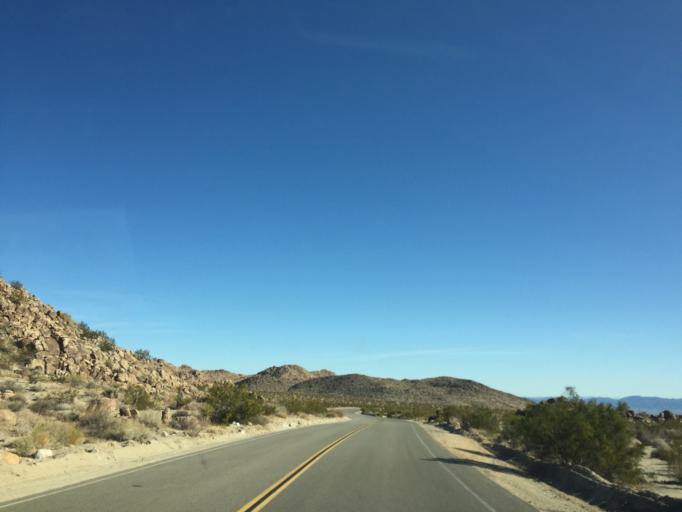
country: US
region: California
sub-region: Riverside County
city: Mecca
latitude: 33.8121
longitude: -115.7687
